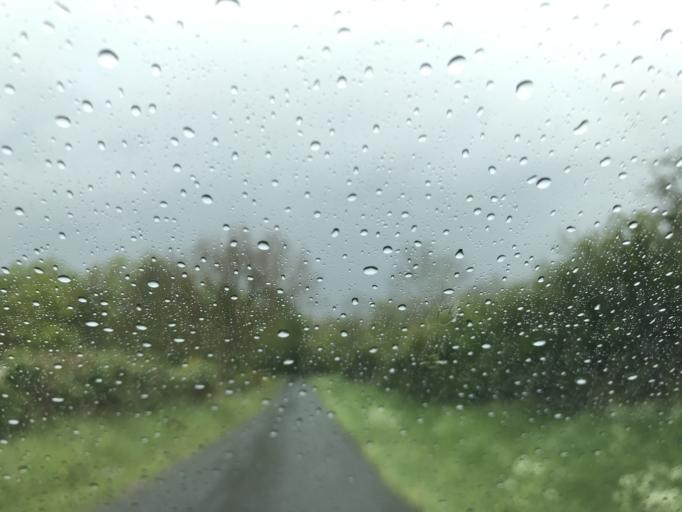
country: FR
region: Auvergne
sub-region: Departement du Puy-de-Dome
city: Courpiere
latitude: 45.7469
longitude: 3.5204
